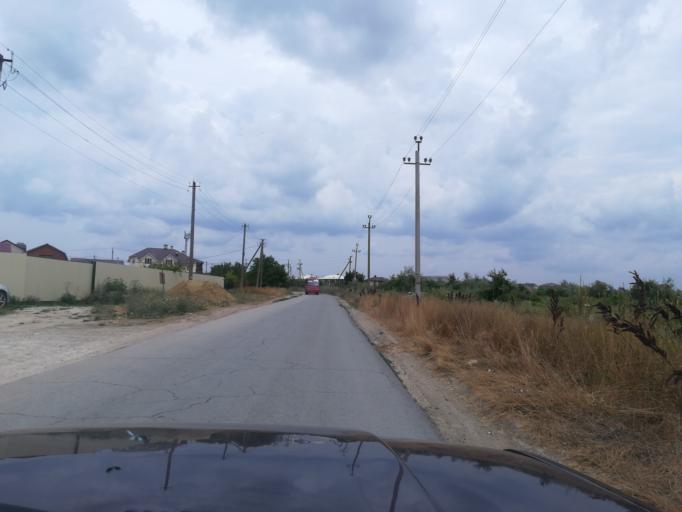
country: RU
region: Krasnodarskiy
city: Vityazevo
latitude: 45.0145
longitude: 37.2955
